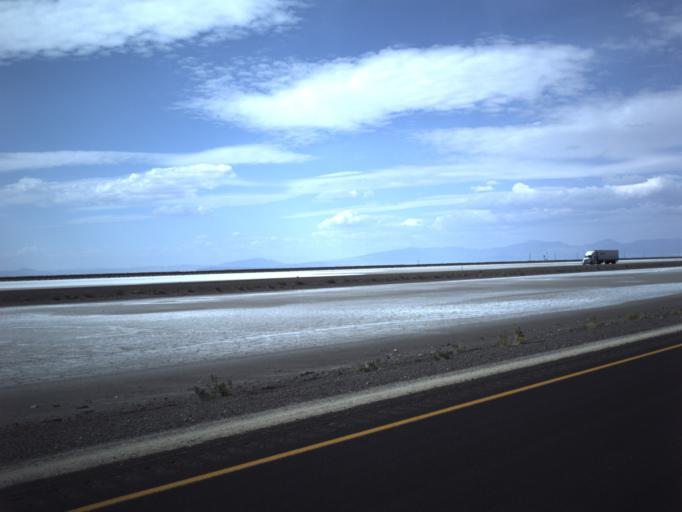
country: US
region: Utah
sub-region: Tooele County
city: Wendover
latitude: 40.7343
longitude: -113.6089
